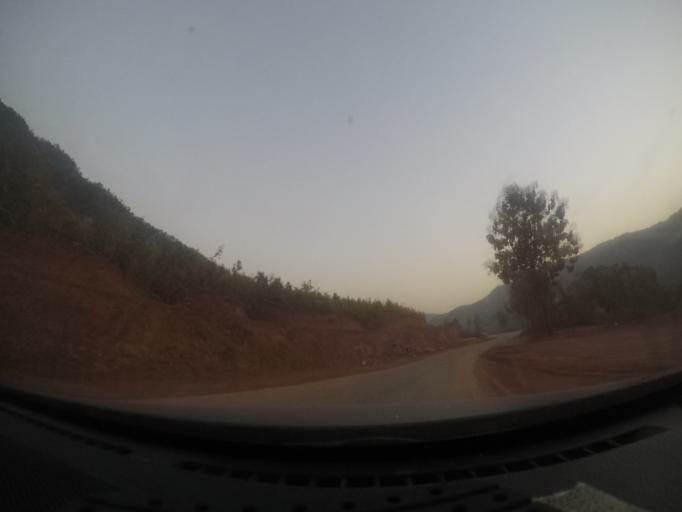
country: MM
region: Mandalay
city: Yamethin
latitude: 20.7183
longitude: 96.4995
